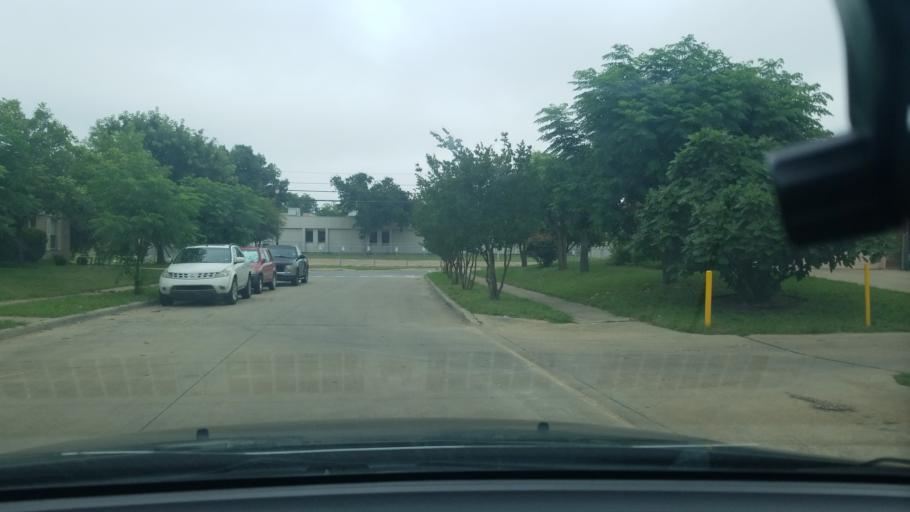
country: US
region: Texas
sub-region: Dallas County
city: Balch Springs
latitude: 32.7573
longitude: -96.6874
